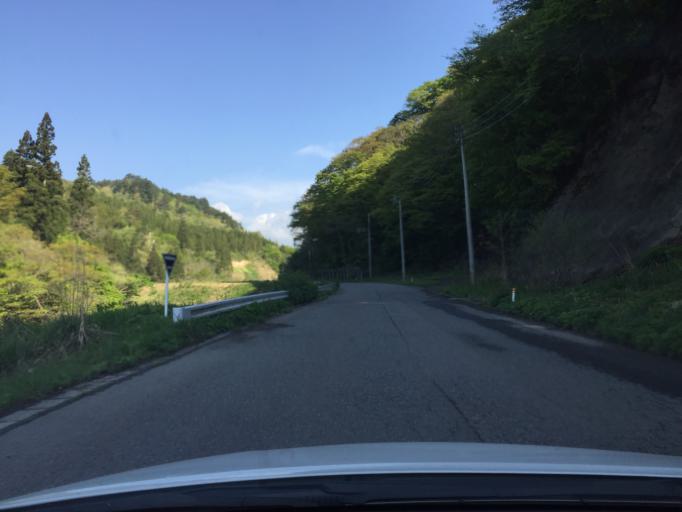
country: JP
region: Fukushima
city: Kitakata
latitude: 37.6720
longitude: 139.7300
